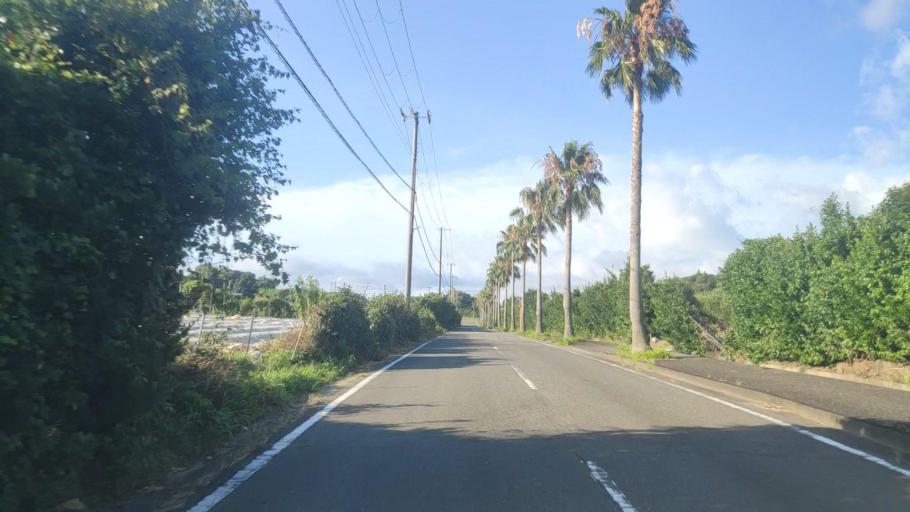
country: JP
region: Wakayama
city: Tanabe
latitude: 33.7709
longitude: 135.3051
